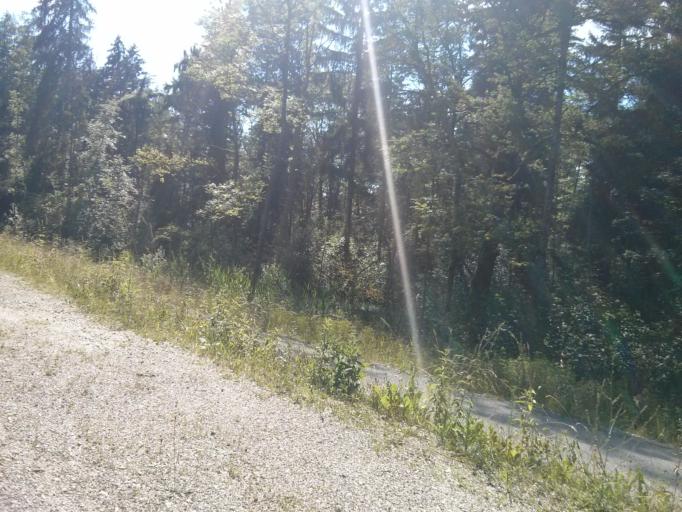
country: DE
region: Bavaria
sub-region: Lower Bavaria
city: Moos
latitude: 48.7890
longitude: 12.9461
